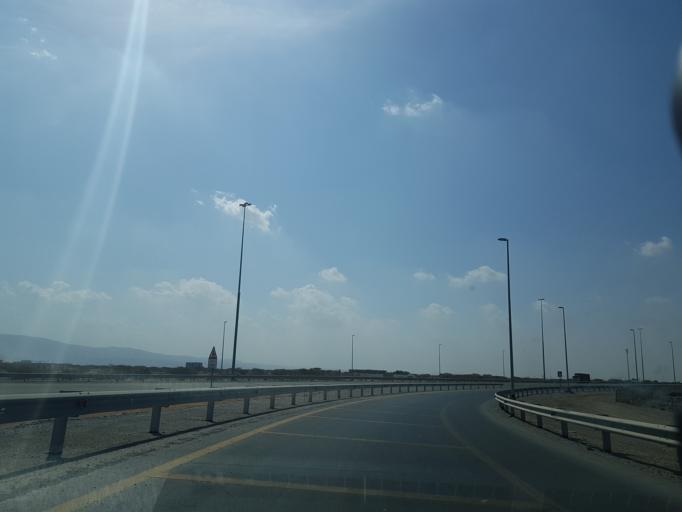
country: AE
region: Ra's al Khaymah
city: Ras al-Khaimah
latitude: 25.7164
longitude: 56.0056
